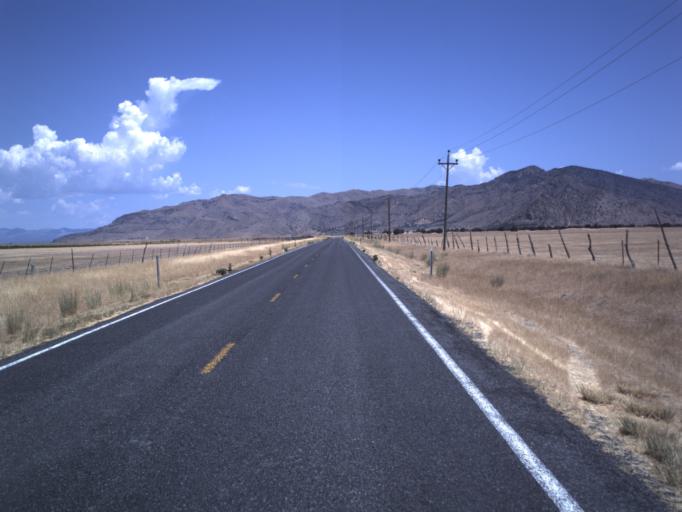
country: US
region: Utah
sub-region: Millard County
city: Delta
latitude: 39.5029
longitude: -112.2690
